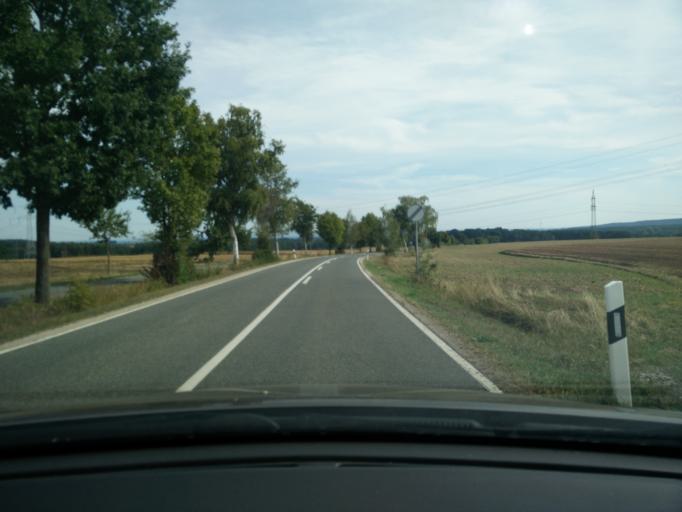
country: DE
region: Bavaria
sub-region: Regierungsbezirk Mittelfranken
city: Tuchenbach
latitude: 49.5183
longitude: 10.8567
